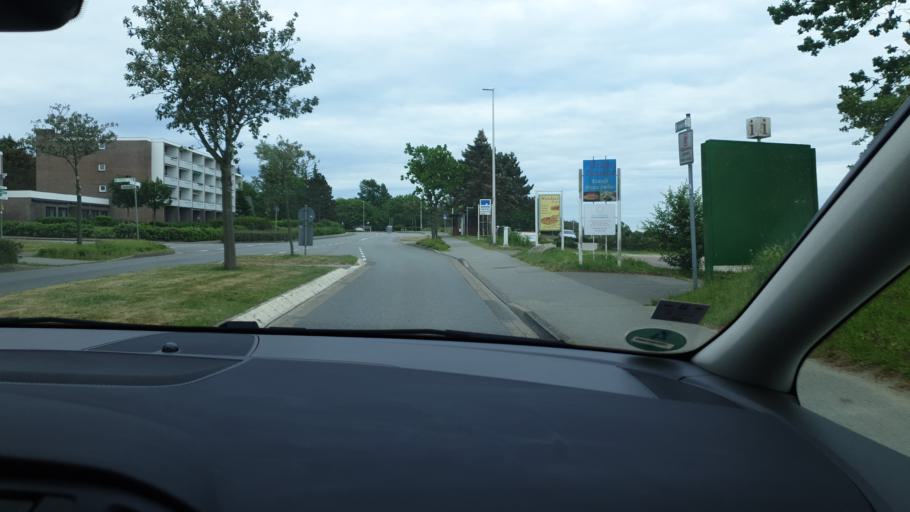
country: DE
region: Schleswig-Holstein
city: Schobull
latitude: 54.5098
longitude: 9.0035
